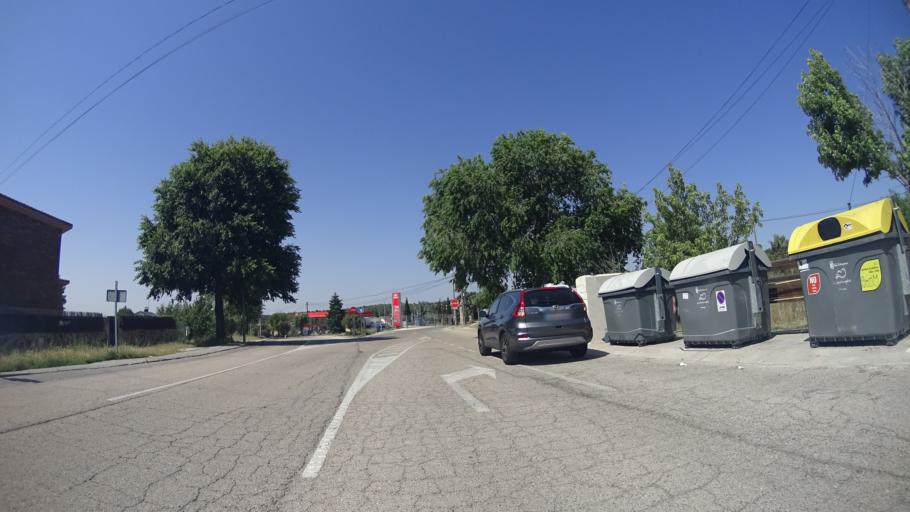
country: ES
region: Madrid
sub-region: Provincia de Madrid
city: Hoyo de Manzanares
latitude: 40.6057
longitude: -3.9036
